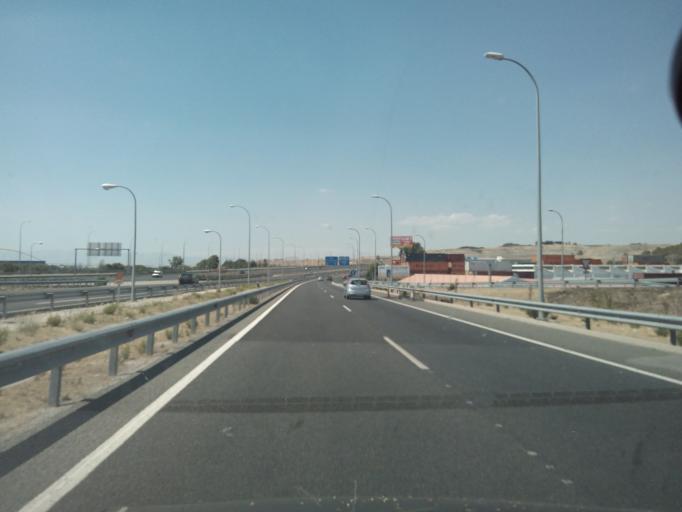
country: ES
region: Madrid
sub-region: Provincia de Madrid
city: San Fernando de Henares
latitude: 40.4527
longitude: -3.5187
